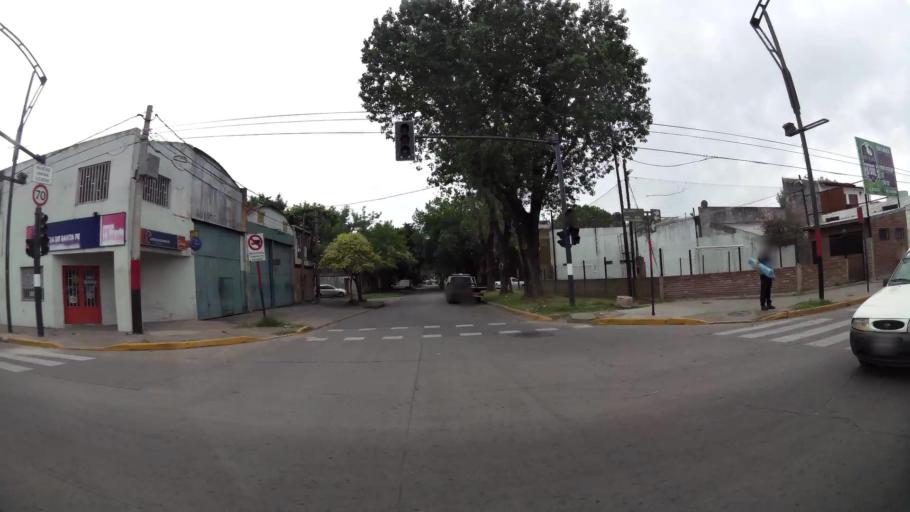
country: AR
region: Santa Fe
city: Gobernador Galvez
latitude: -32.9946
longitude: -60.6655
